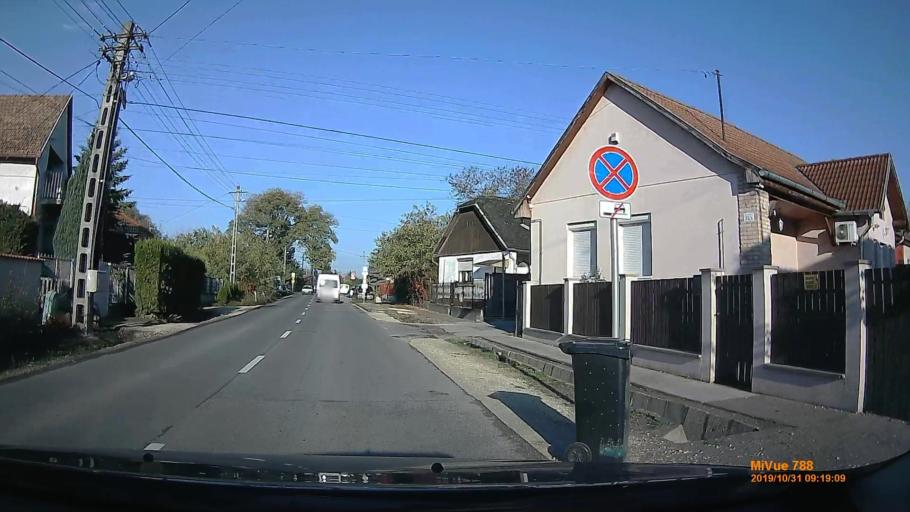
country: HU
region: Pest
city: Gyomro
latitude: 47.4162
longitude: 19.3937
